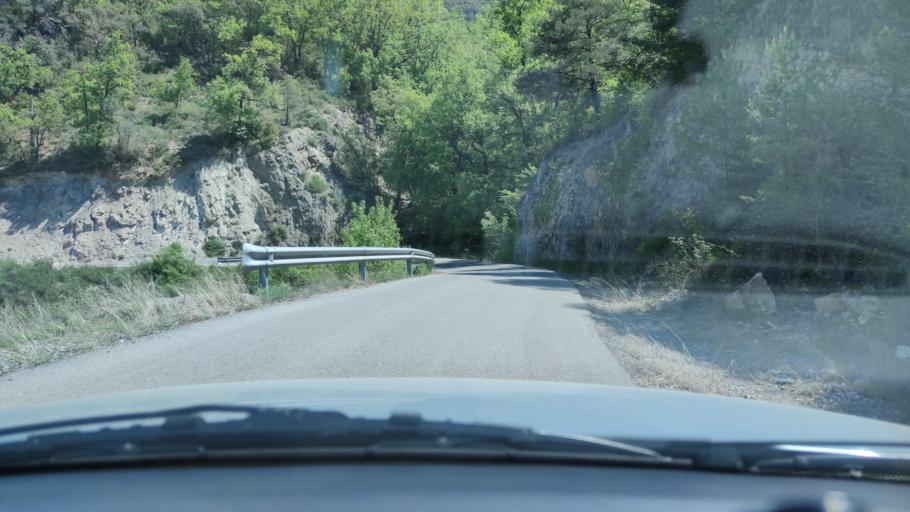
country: ES
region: Catalonia
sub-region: Provincia de Lleida
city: Sort
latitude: 42.3127
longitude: 1.0659
